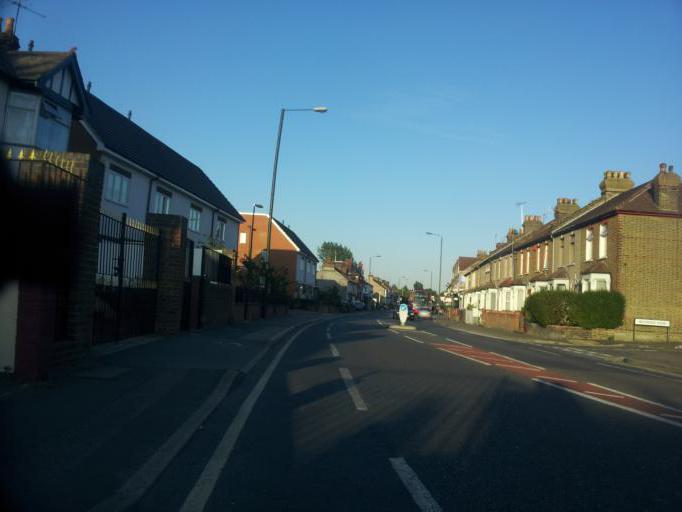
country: GB
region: England
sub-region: Greater London
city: Belvedere
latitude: 51.4905
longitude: 0.1602
